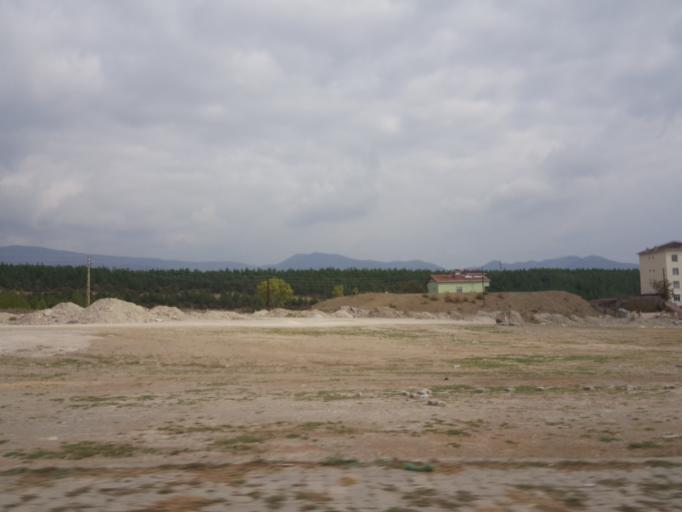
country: TR
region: Sinop
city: Duragan
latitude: 41.4291
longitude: 35.0537
